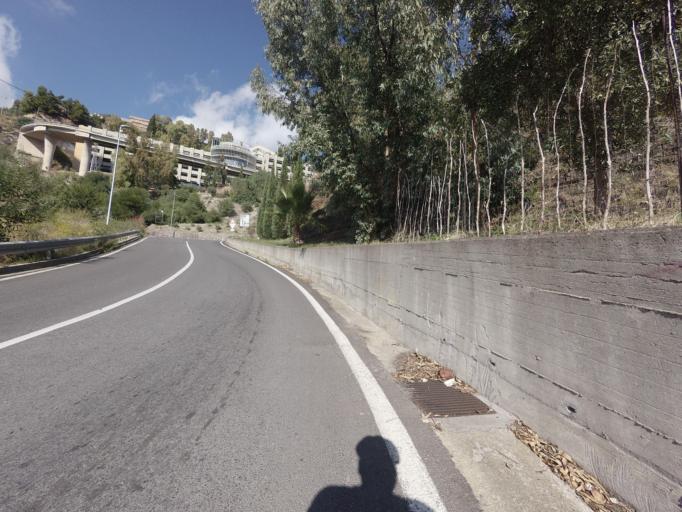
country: IT
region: Sicily
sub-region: Messina
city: Castelmola
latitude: 37.8495
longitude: 15.2797
